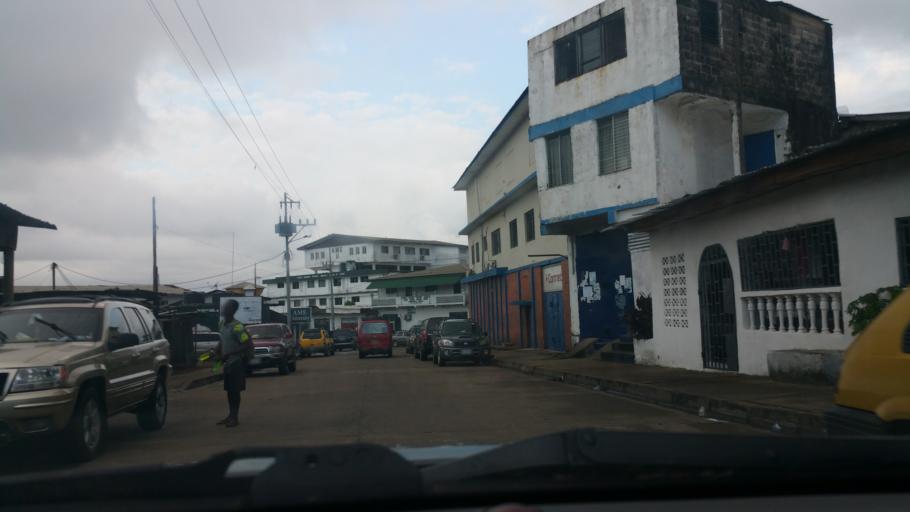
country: LR
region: Montserrado
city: Monrovia
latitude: 6.3118
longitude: -10.8008
